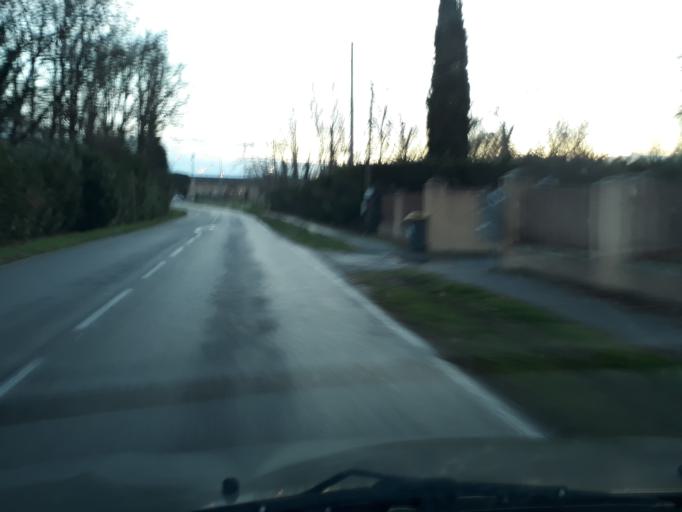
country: FR
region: Midi-Pyrenees
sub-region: Departement de la Haute-Garonne
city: Carbonne
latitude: 43.3111
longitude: 1.2315
